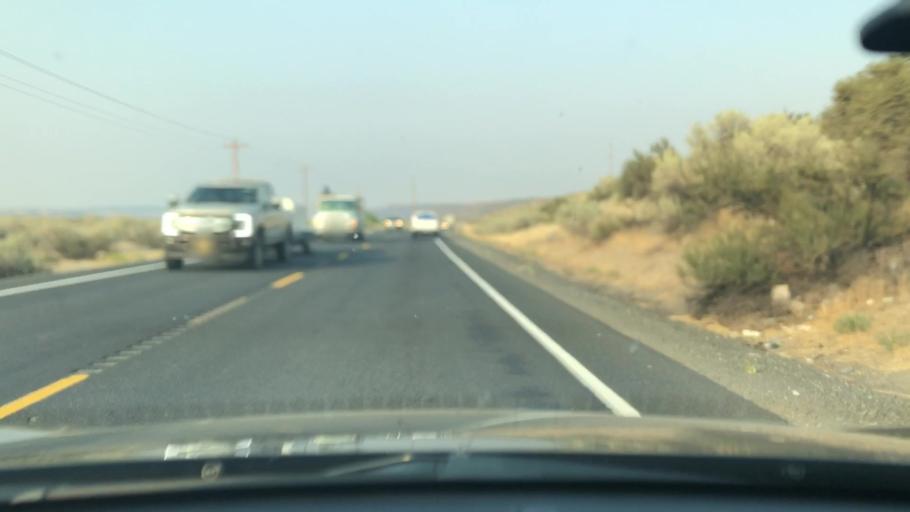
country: US
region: Oregon
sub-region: Umatilla County
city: Stanfield
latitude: 45.9195
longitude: -119.1249
